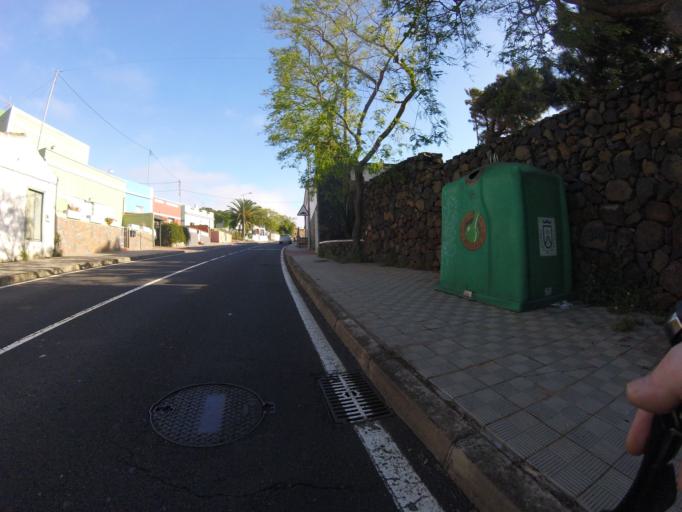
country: ES
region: Canary Islands
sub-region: Provincia de Santa Cruz de Tenerife
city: La Laguna
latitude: 28.4681
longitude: -16.3169
